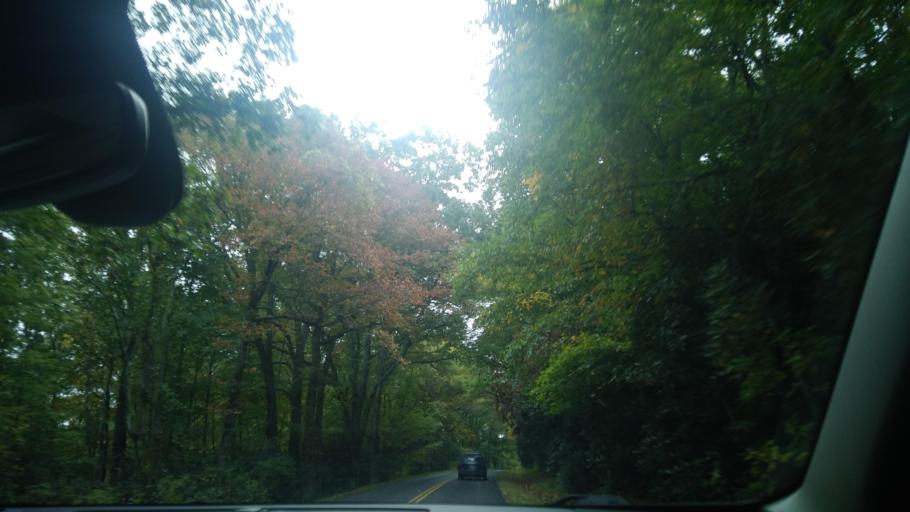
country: US
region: Virginia
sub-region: Carroll County
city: Cana
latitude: 36.6670
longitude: -80.6075
